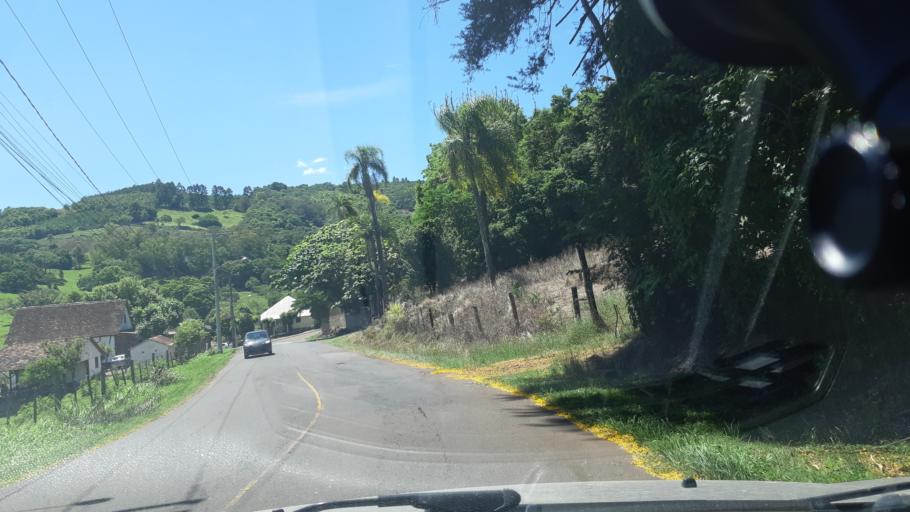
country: BR
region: Rio Grande do Sul
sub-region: Novo Hamburgo
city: Novo Hamburgo
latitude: -29.6270
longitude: -51.0958
